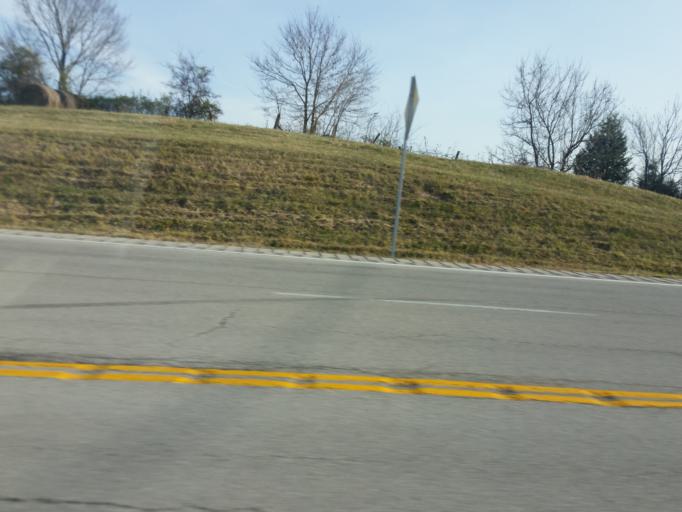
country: US
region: Kentucky
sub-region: Harrison County
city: Cynthiana
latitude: 38.5191
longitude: -84.2888
